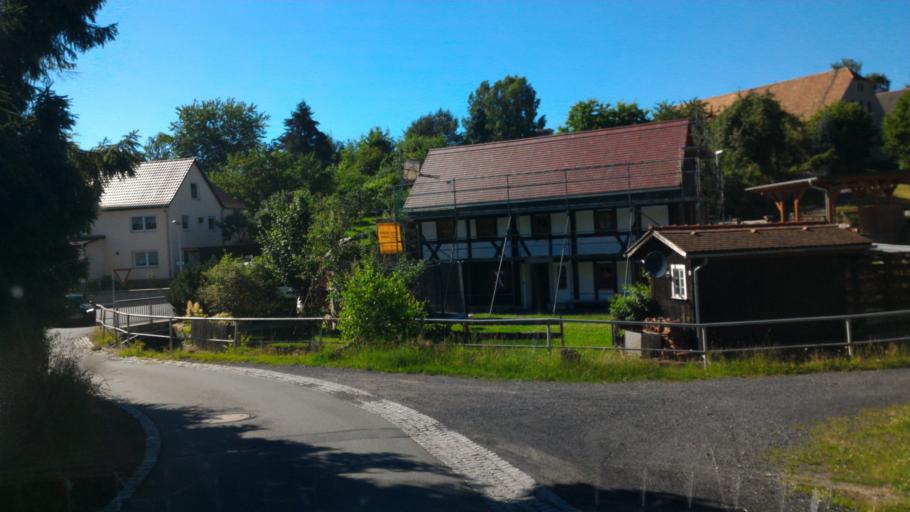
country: DE
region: Saxony
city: Mittelherwigsdorf
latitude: 50.9167
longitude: 14.7642
